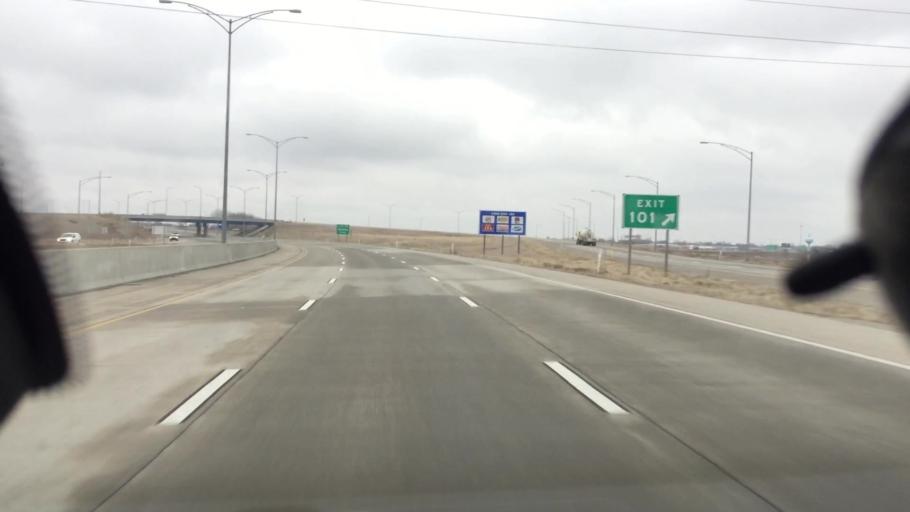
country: US
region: Illinois
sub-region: Tazewell County
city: Morton
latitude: 40.6215
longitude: -89.4888
